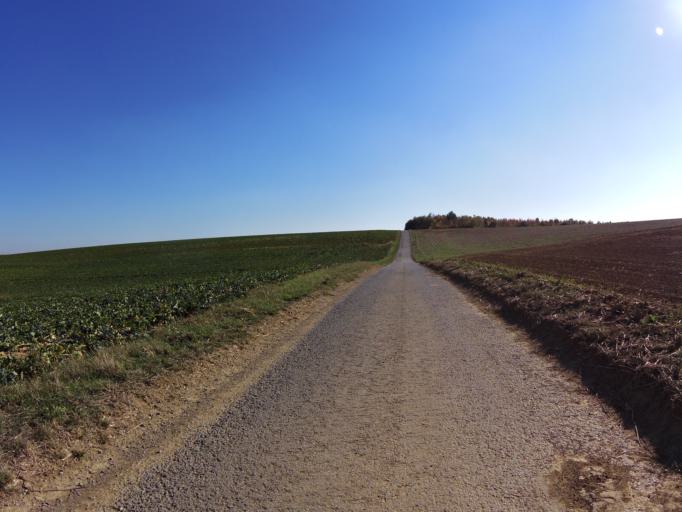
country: DE
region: Bavaria
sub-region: Regierungsbezirk Unterfranken
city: Eibelstadt
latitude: 49.7099
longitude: 9.9817
